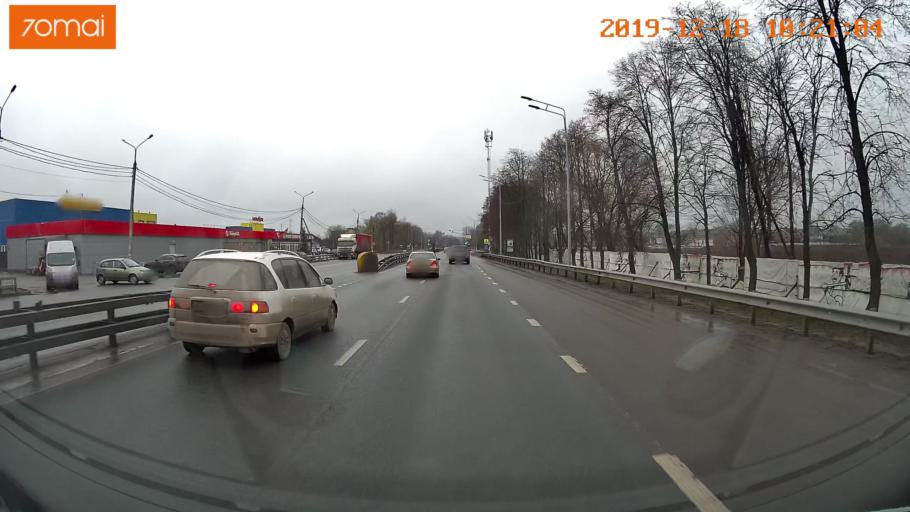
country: RU
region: Moskovskaya
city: Dubrovitsy
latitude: 55.3895
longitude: 37.4232
